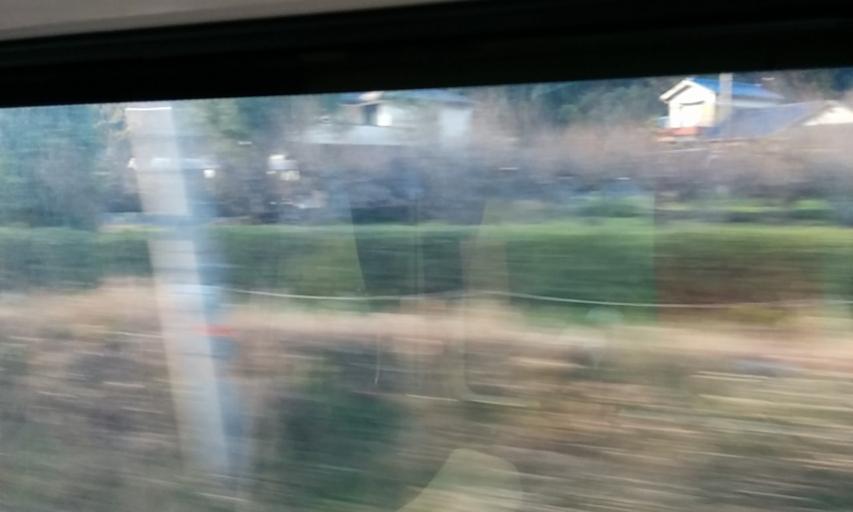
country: JP
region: Aichi
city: Seto
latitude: 35.2693
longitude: 137.0729
